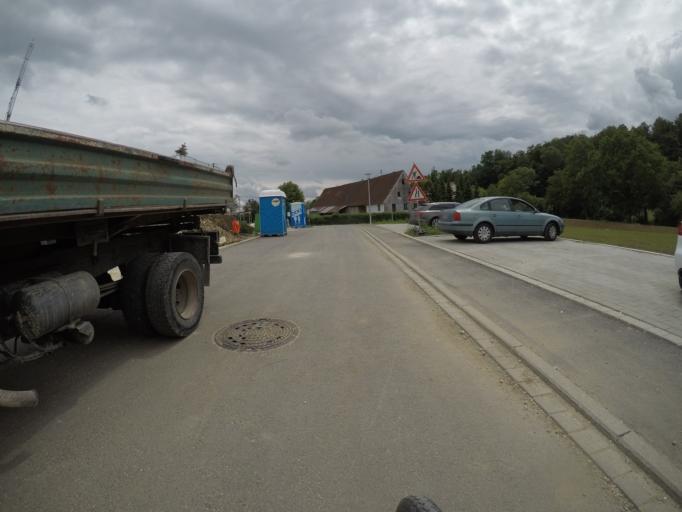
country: DE
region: Baden-Wuerttemberg
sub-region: Tuebingen Region
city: Lonsee
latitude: 48.5415
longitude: 9.9188
